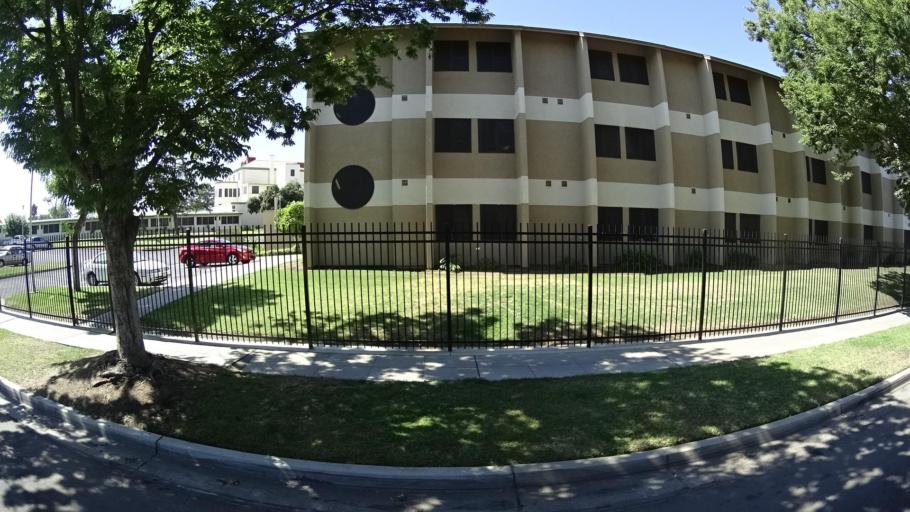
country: US
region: California
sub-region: Fresno County
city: Fresno
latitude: 36.7630
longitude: -119.8189
